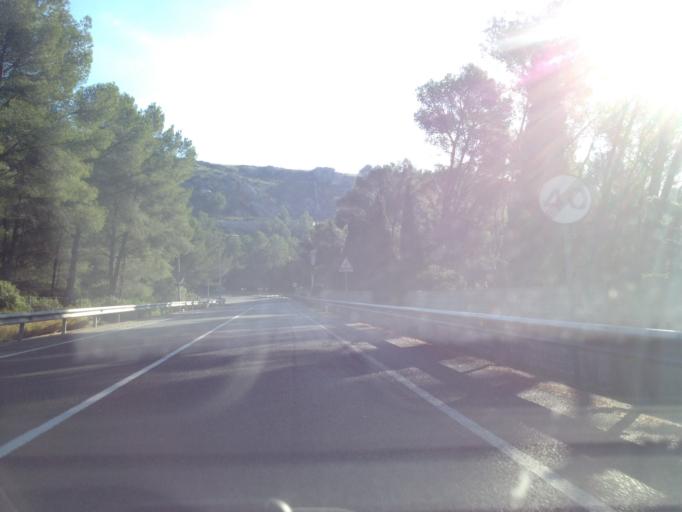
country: ES
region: Balearic Islands
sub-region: Illes Balears
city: Alcudia
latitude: 39.9126
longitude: 3.1003
